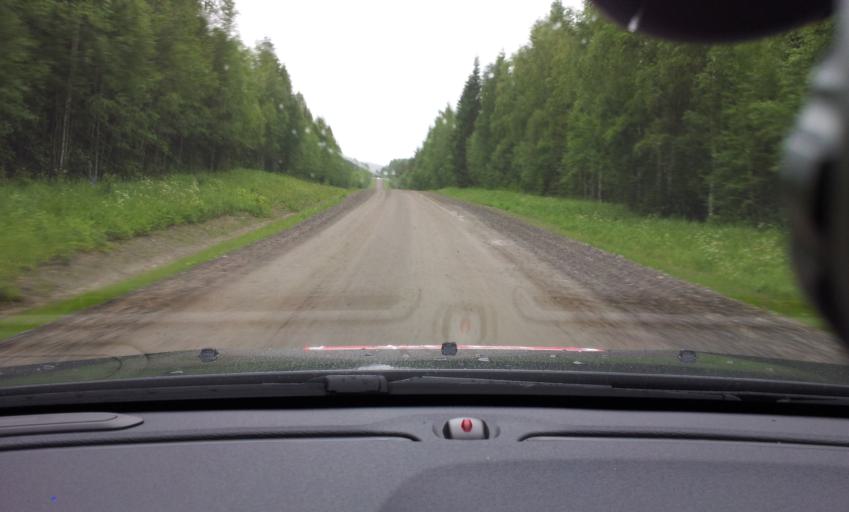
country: SE
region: Jaemtland
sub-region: Ragunda Kommun
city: Hammarstrand
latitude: 63.1240
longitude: 16.3286
